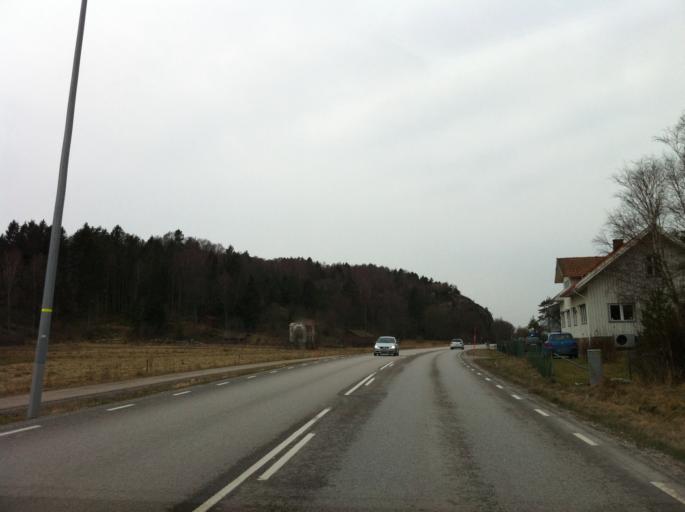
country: SE
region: Vaestra Goetaland
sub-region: Orust
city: Henan
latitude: 58.2234
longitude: 11.6865
